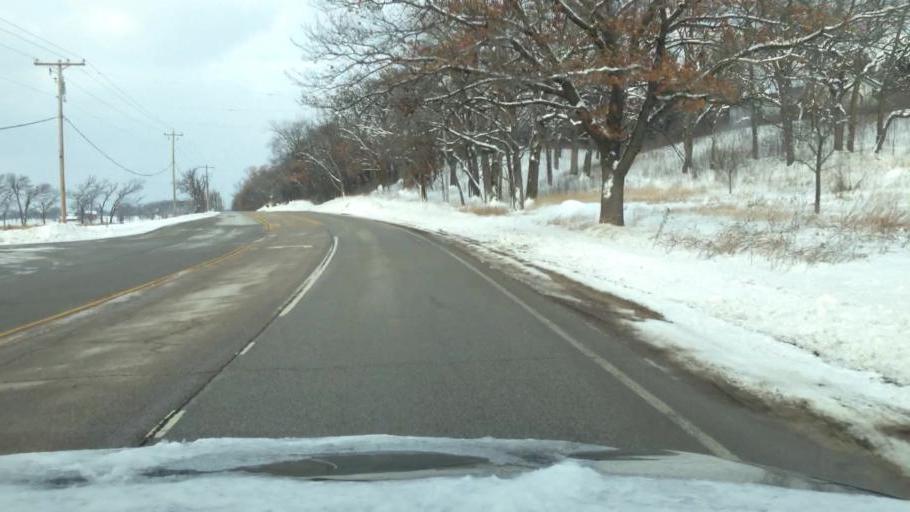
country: US
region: Wisconsin
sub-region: Waukesha County
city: North Prairie
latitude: 42.8898
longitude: -88.4171
